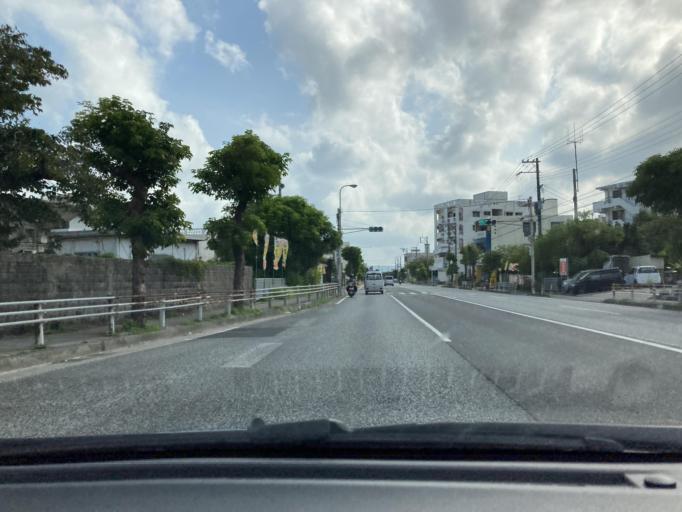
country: JP
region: Okinawa
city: Ginowan
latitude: 26.2679
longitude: 127.7908
